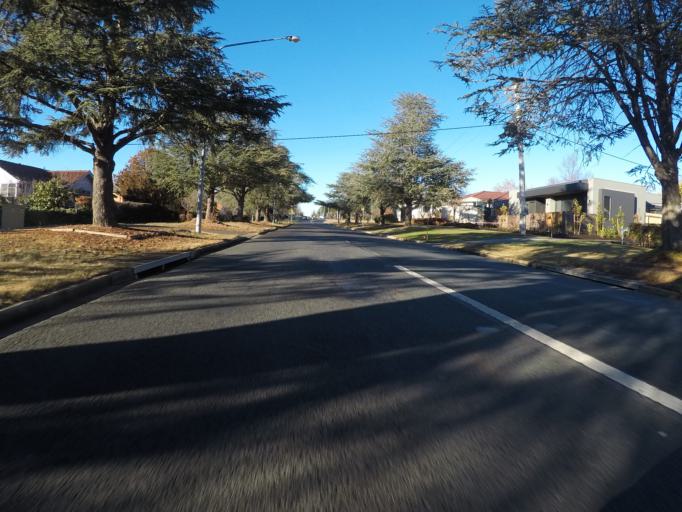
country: AU
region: Australian Capital Territory
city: Forrest
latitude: -35.3114
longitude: 149.0983
